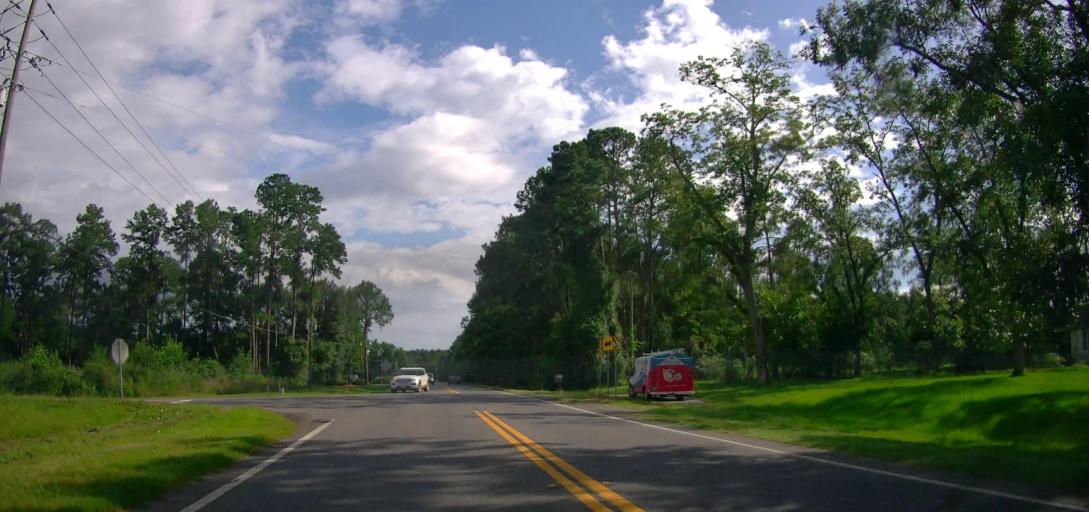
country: US
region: Georgia
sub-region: Coffee County
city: Douglas
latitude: 31.4516
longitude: -82.8883
